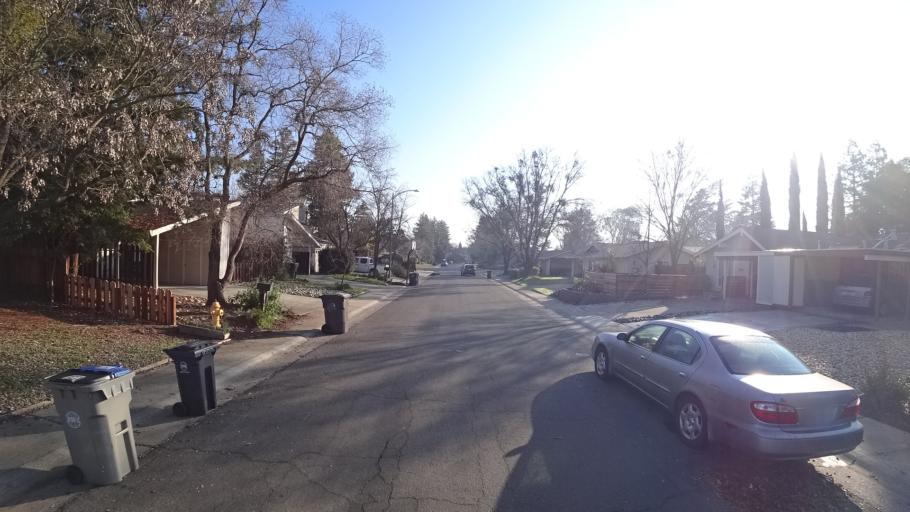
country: US
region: California
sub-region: Yolo County
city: Davis
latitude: 38.5552
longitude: -121.7930
